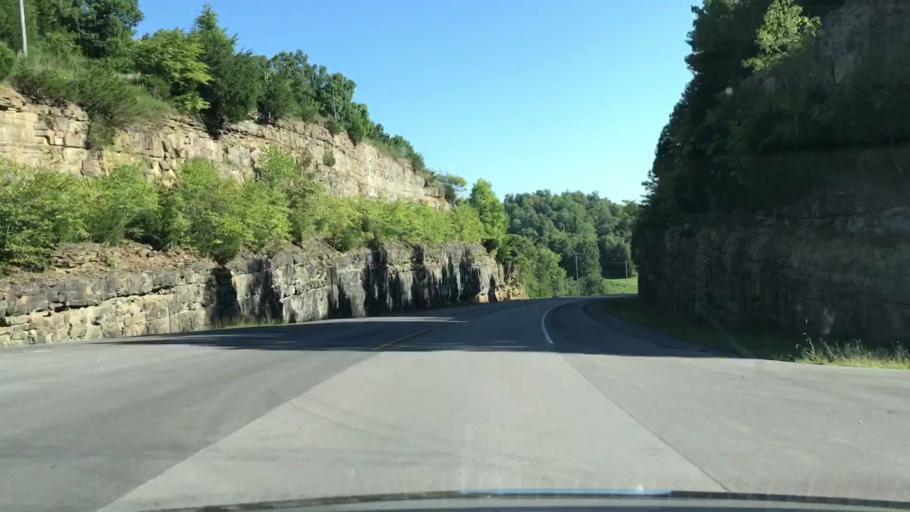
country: US
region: Kentucky
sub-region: Cumberland County
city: Burkesville
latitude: 36.7040
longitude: -85.3716
